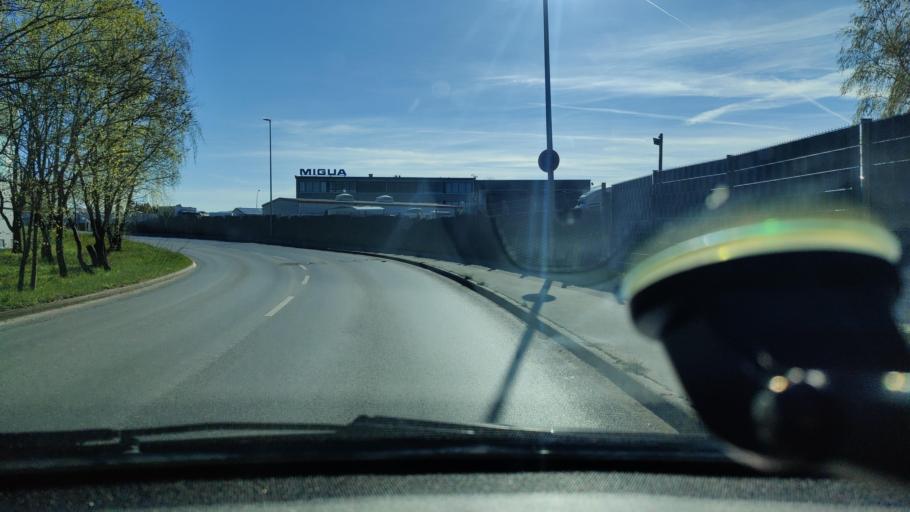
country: DE
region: North Rhine-Westphalia
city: Wulfrath
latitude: 51.2980
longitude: 7.0580
